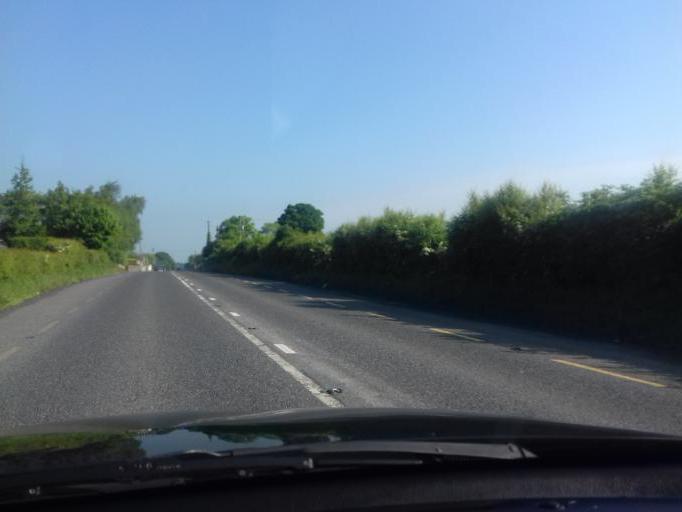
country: IE
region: Leinster
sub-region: Dublin City
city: Finglas
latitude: 53.4298
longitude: -6.3309
